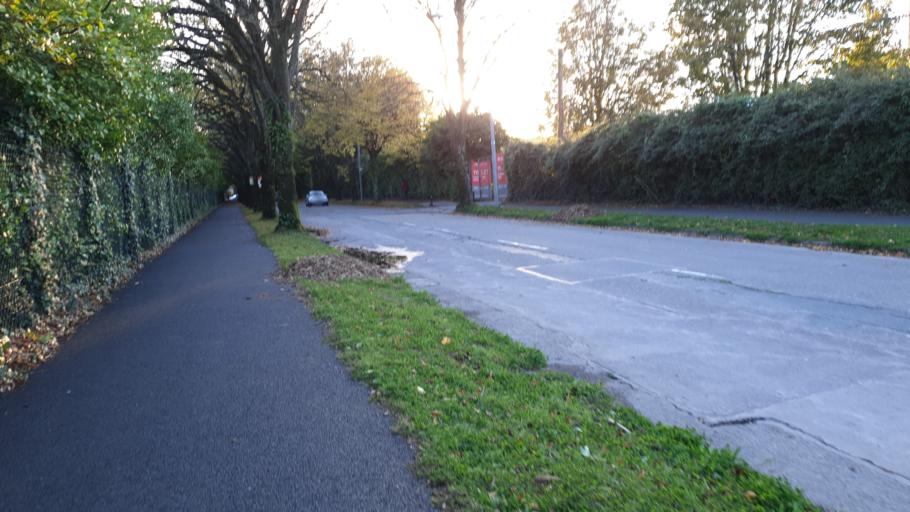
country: IE
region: Munster
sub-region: County Cork
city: Cork
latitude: 51.8999
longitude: -8.4407
